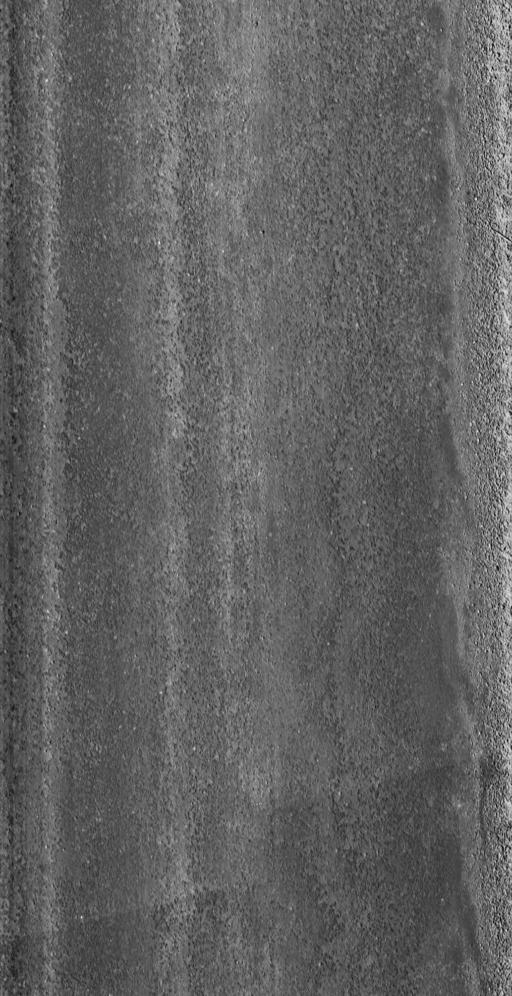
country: US
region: Vermont
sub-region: Washington County
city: South Barre
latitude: 44.1468
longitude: -72.4933
